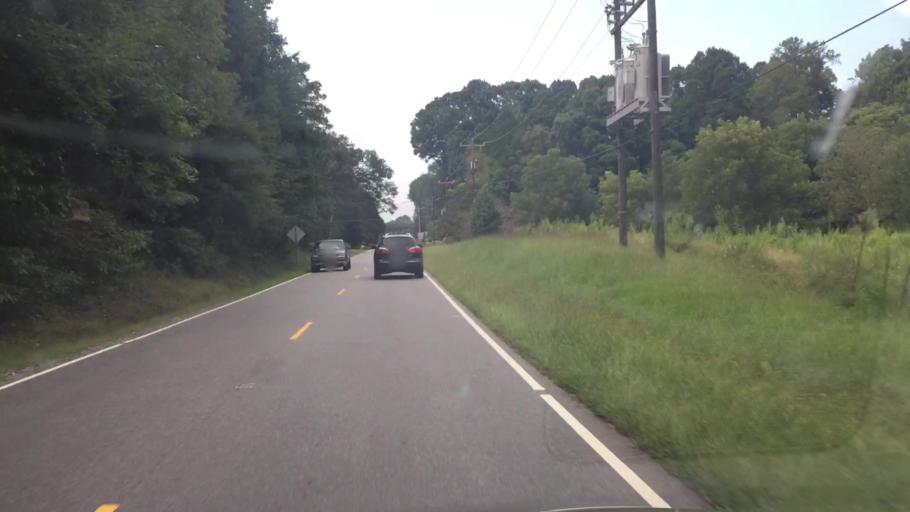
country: US
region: North Carolina
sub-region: Iredell County
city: Mooresville
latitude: 35.6039
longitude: -80.7944
